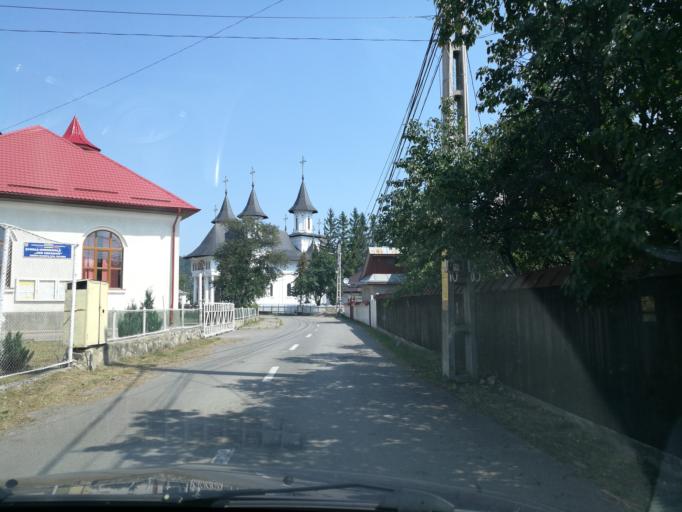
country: RO
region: Neamt
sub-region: Oras Targu Neamt
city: Humulesti
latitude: 47.1976
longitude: 26.3518
